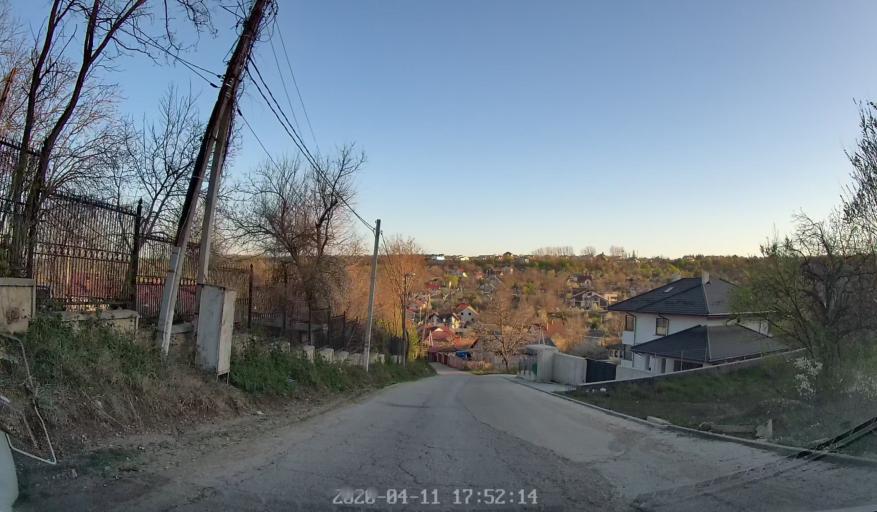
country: MD
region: Chisinau
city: Chisinau
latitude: 46.9735
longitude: 28.8640
